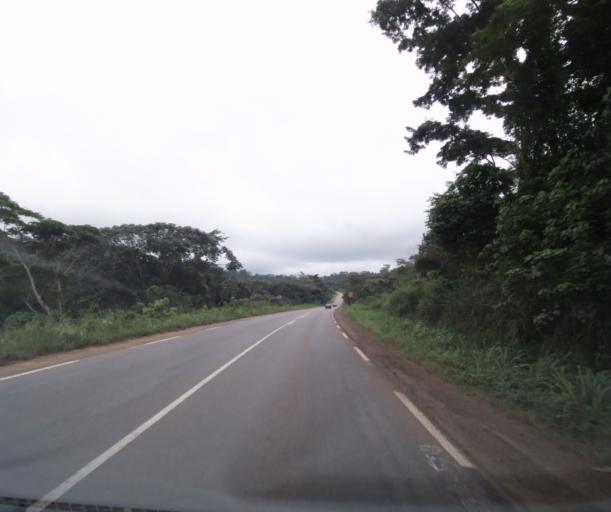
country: CM
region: Centre
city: Mbankomo
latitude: 3.7817
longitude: 11.2765
